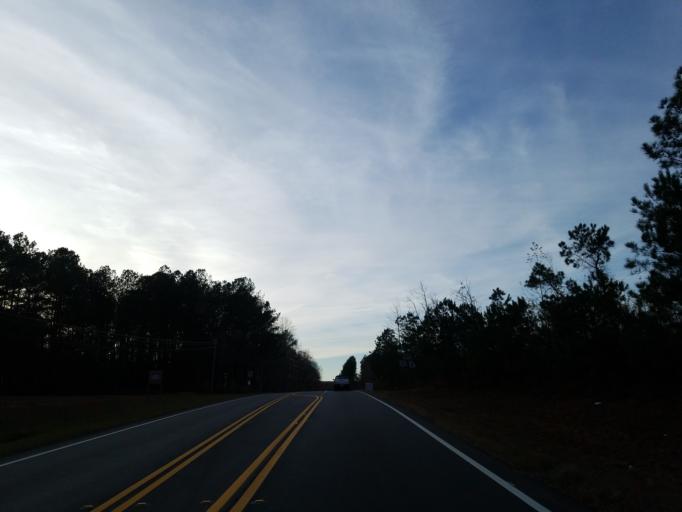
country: US
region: Georgia
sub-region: Carroll County
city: Temple
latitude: 33.7324
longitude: -85.0507
